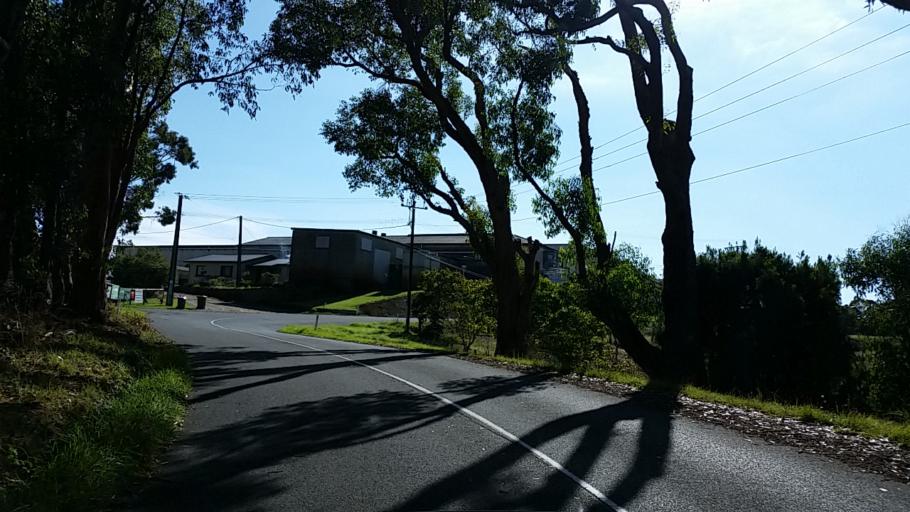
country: AU
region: South Australia
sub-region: Adelaide Hills
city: Adelaide Hills
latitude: -34.9441
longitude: 138.7272
